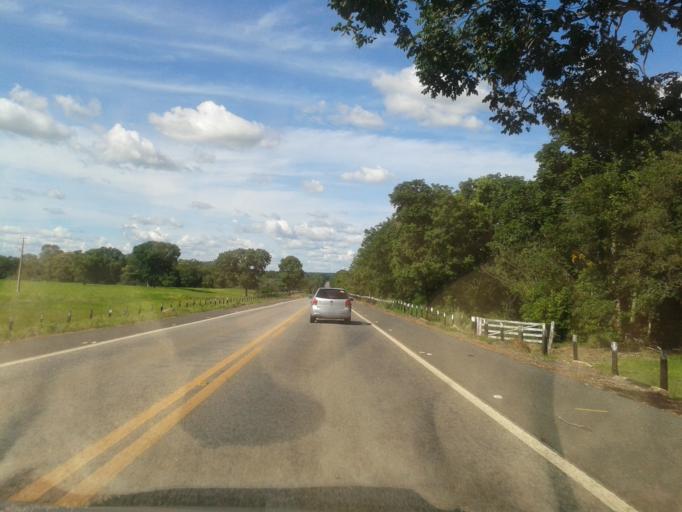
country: BR
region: Goias
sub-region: Mozarlandia
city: Mozarlandia
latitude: -15.0060
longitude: -50.5912
